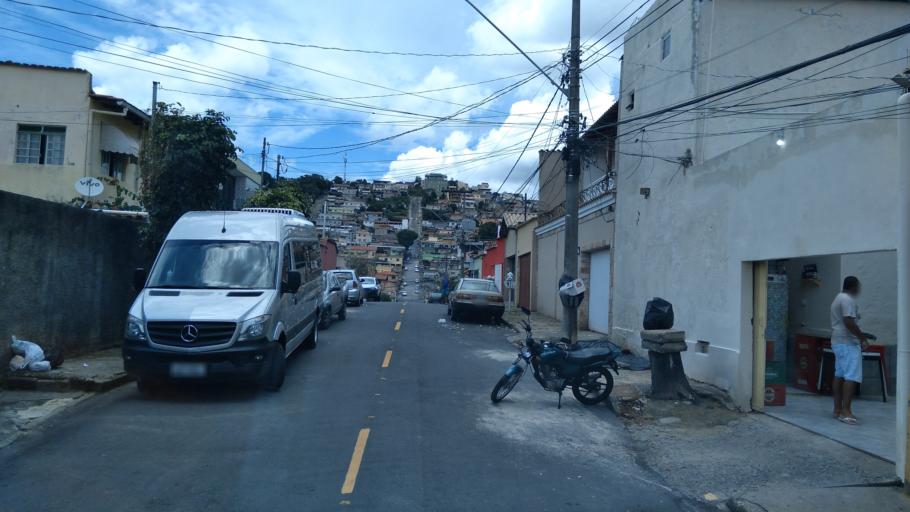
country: BR
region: Minas Gerais
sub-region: Belo Horizonte
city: Belo Horizonte
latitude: -19.9205
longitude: -43.9032
